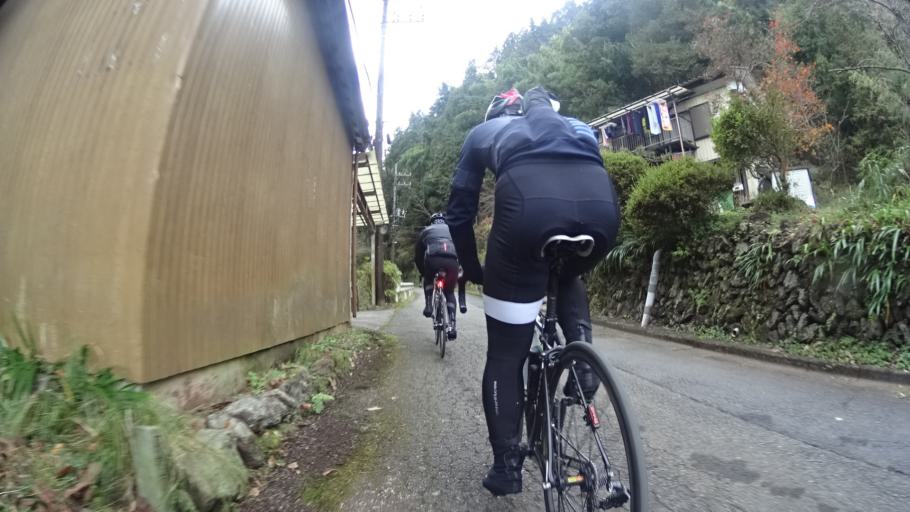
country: JP
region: Saitama
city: Morohongo
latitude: 35.9125
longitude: 139.2153
